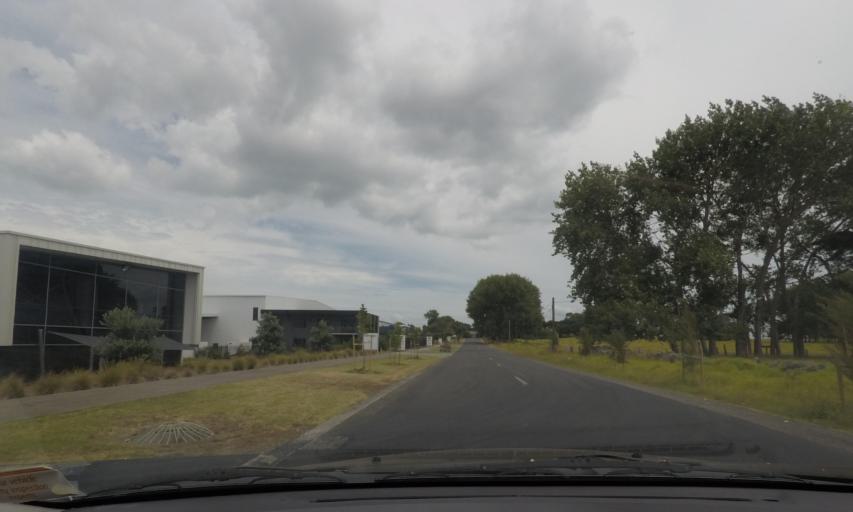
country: NZ
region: Auckland
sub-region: Auckland
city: Mangere
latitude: -36.9897
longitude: 174.7598
